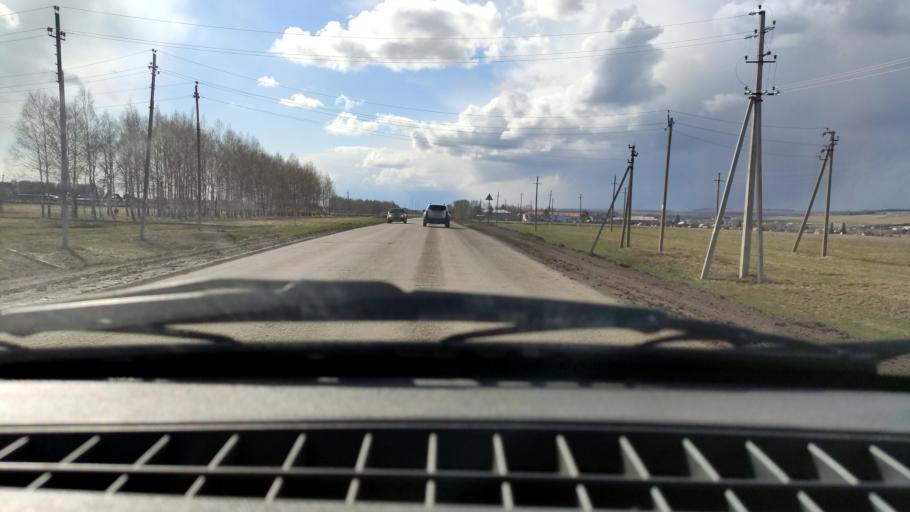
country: RU
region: Bashkortostan
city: Chekmagush
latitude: 55.1150
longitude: 54.8573
